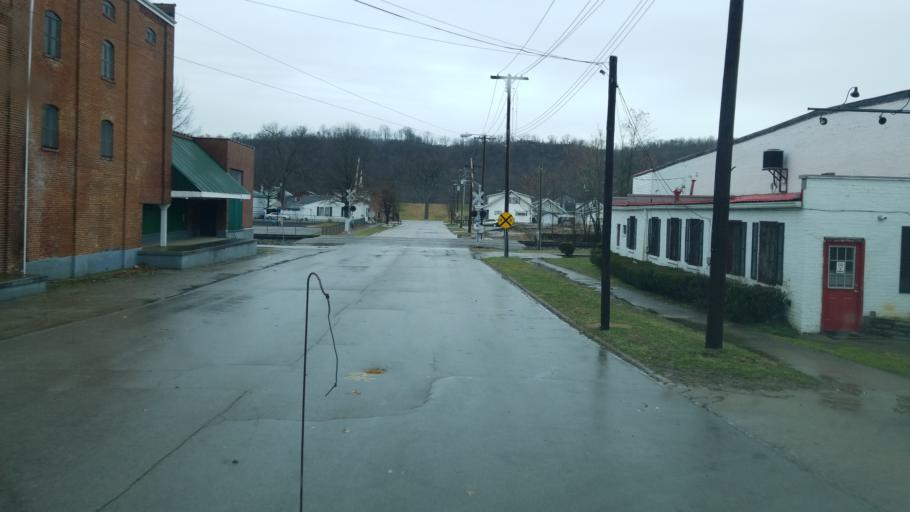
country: US
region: Kentucky
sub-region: Mason County
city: Maysville
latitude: 38.6425
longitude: -83.7486
